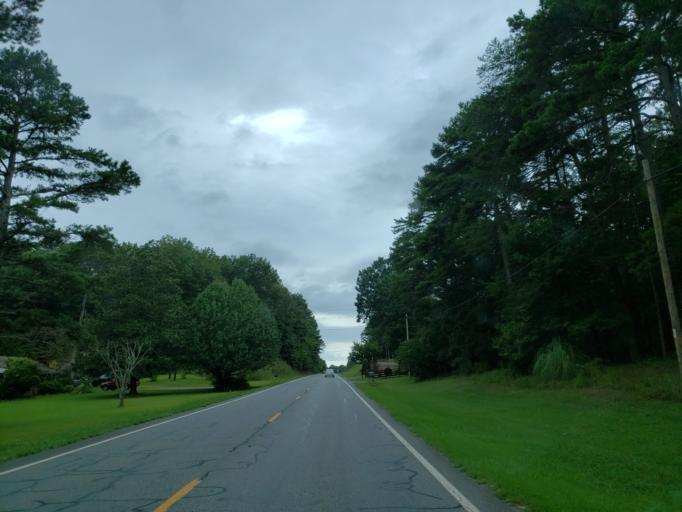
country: US
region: Georgia
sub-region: Gilmer County
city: Ellijay
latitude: 34.6410
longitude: -84.5389
